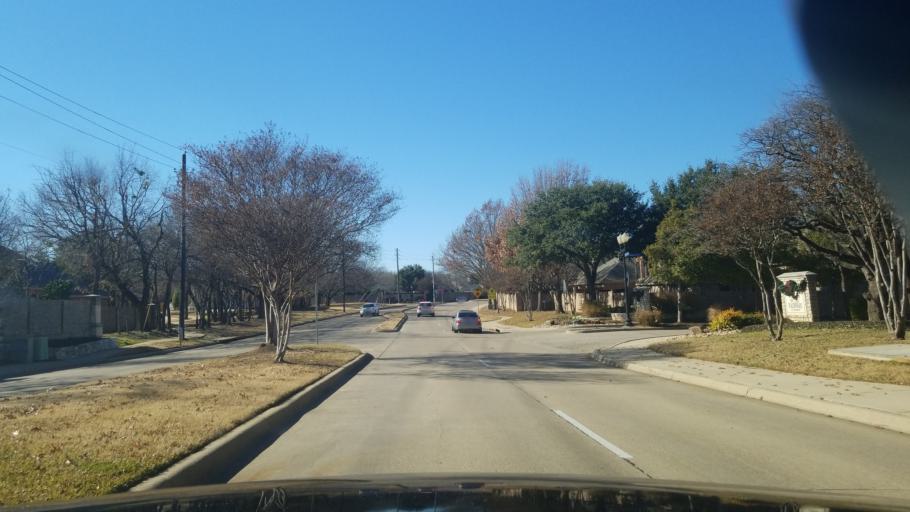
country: US
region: Texas
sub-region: Denton County
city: Corinth
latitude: 33.1552
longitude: -97.0831
